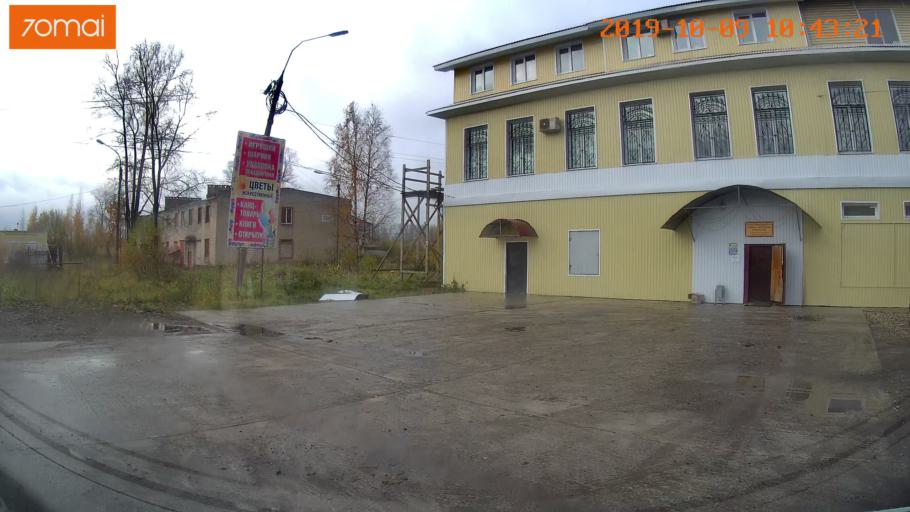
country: RU
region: Vologda
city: Vologda
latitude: 59.2368
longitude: 39.8155
